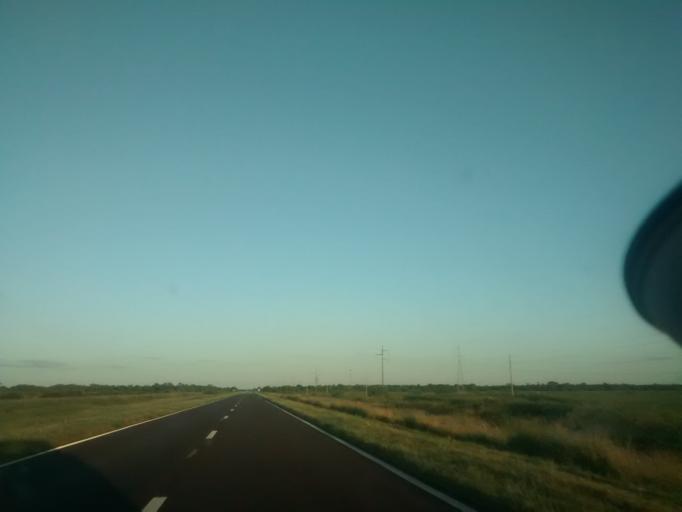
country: AR
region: Chaco
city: La Escondida
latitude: -27.1008
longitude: -59.6068
